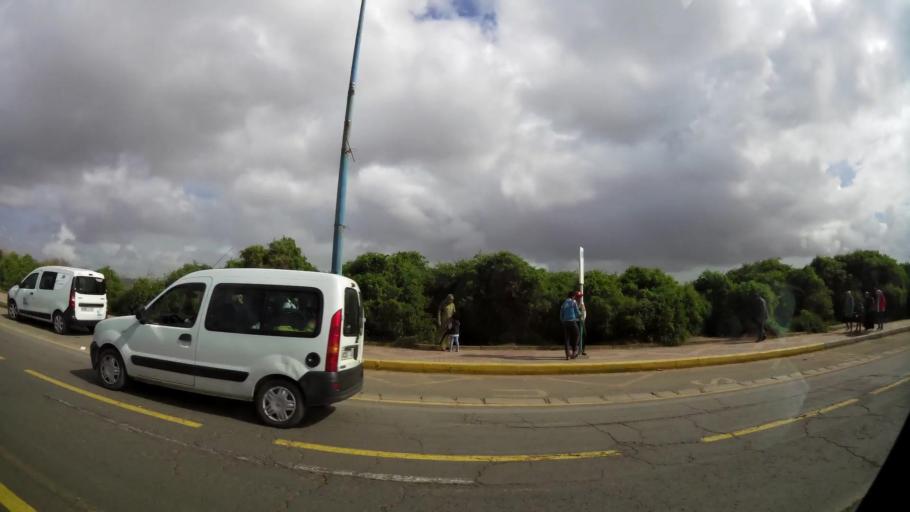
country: MA
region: Grand Casablanca
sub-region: Casablanca
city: Casablanca
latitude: 33.5813
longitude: -7.7021
